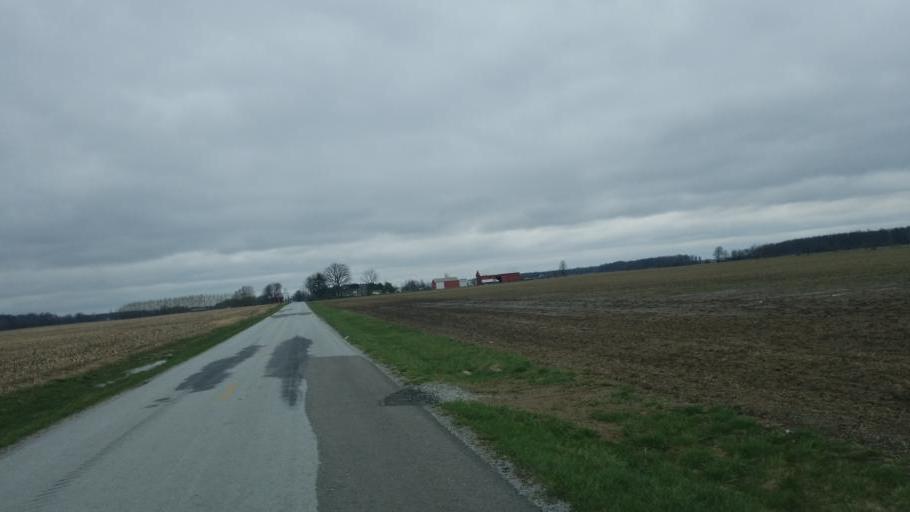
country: US
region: Ohio
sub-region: Hardin County
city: Forest
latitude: 40.7250
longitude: -83.5381
